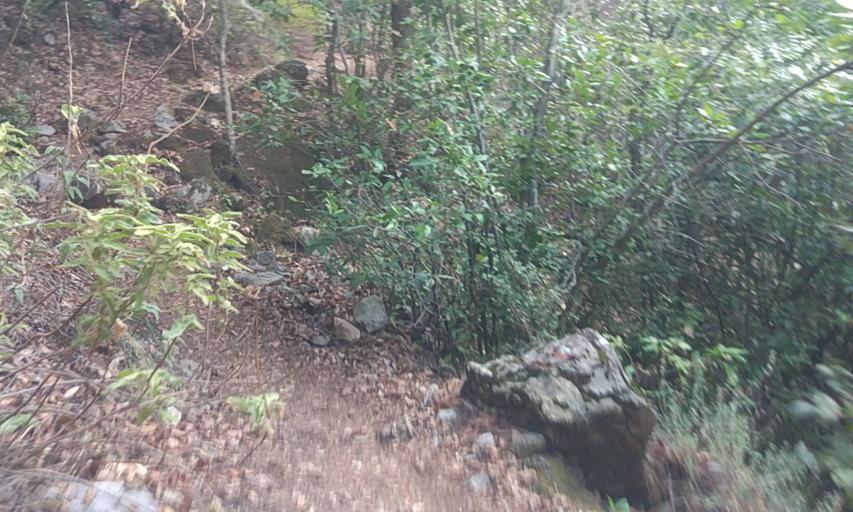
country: TR
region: Antalya
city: Tekirova
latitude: 36.3816
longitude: 30.4758
